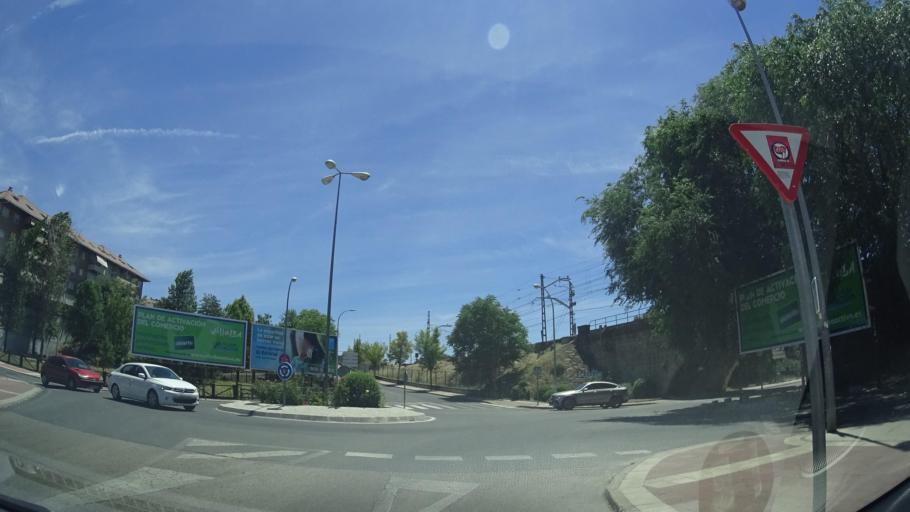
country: ES
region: Madrid
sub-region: Provincia de Madrid
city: Collado-Villalba
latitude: 40.6259
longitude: -4.0038
